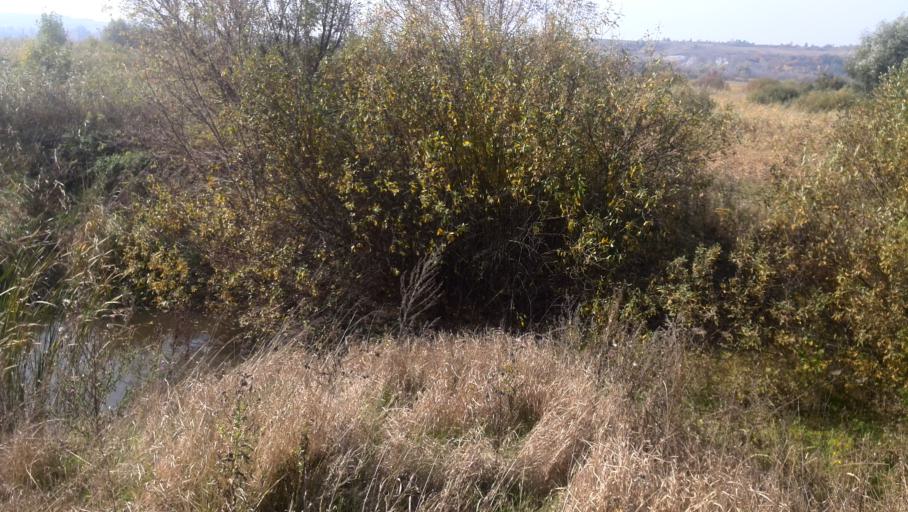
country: RU
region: Voronezj
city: Kalach
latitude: 50.4864
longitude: 41.0051
